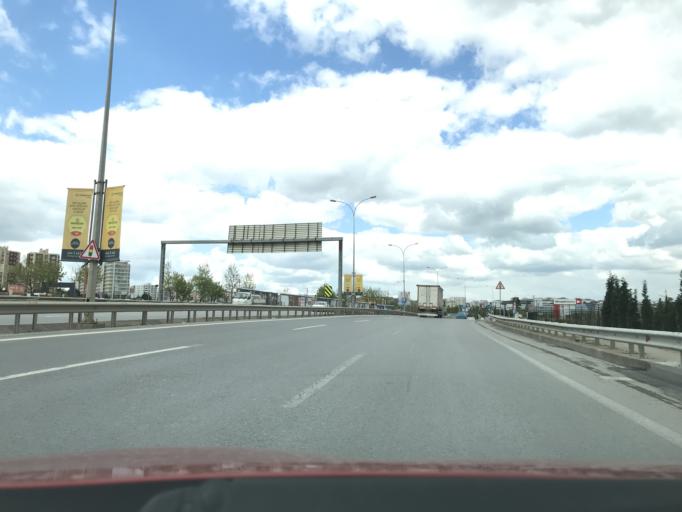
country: TR
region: Istanbul
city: Pendik
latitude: 40.9161
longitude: 29.3121
